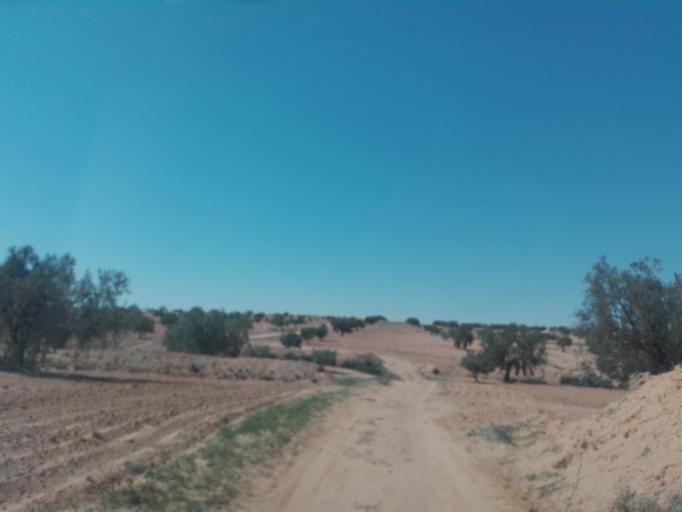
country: TN
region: Safaqis
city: Bi'r `Ali Bin Khalifah
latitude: 34.7976
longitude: 10.2848
